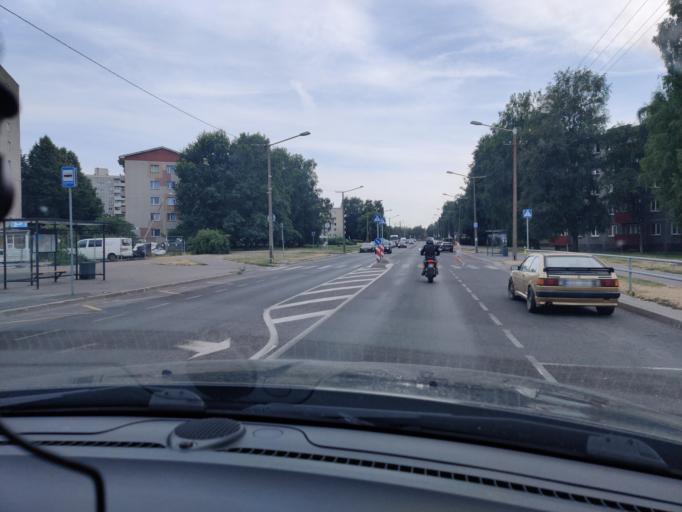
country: EE
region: Harju
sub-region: Tallinna linn
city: Tallinn
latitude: 59.4040
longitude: 24.6802
